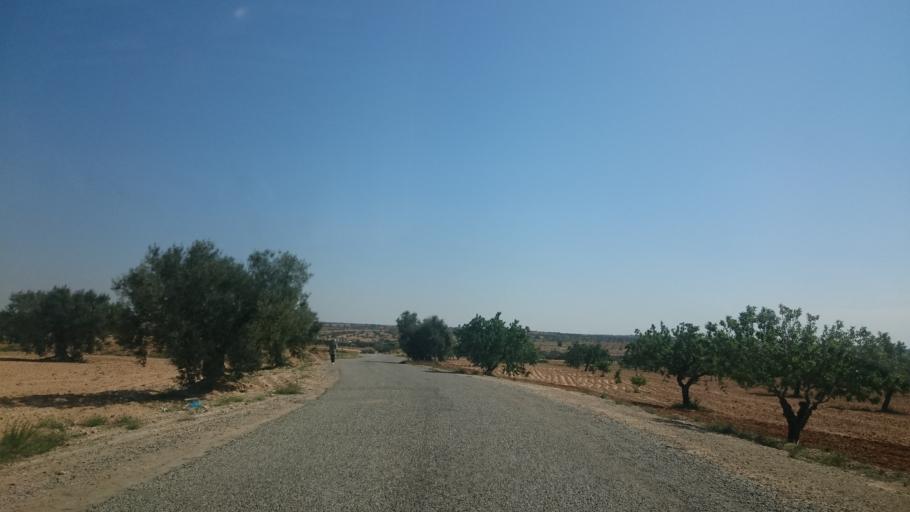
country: TN
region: Safaqis
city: Sfax
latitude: 34.7879
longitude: 10.5181
